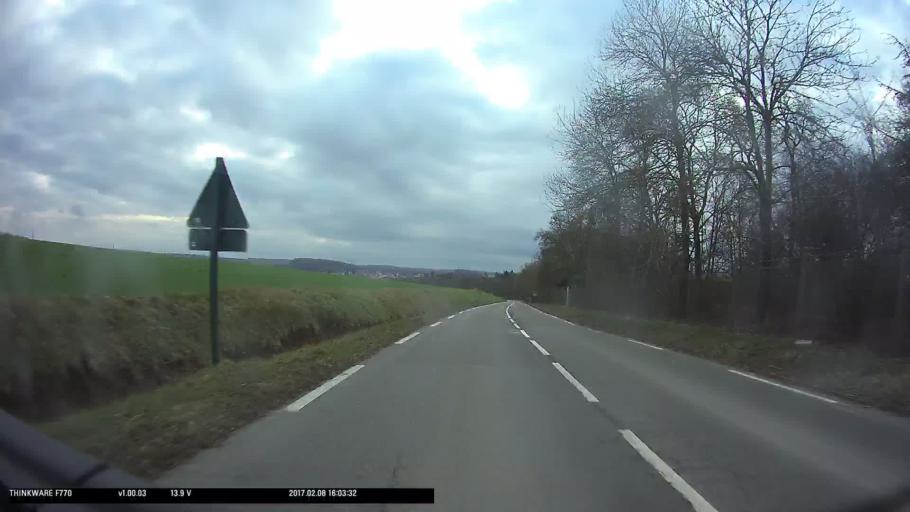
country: FR
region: Ile-de-France
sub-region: Departement du Val-d'Oise
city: Us
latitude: 49.1092
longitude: 1.9756
